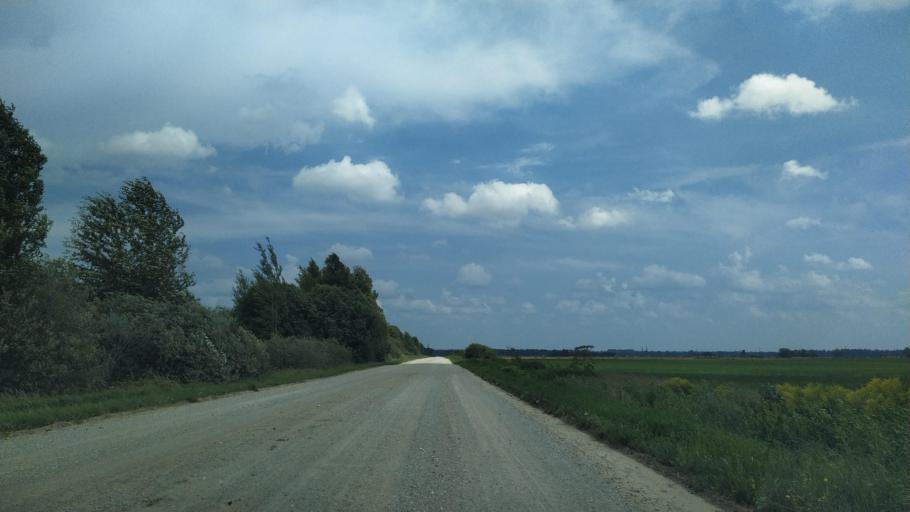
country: RU
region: Pskov
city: Pskov
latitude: 57.5851
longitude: 28.3251
